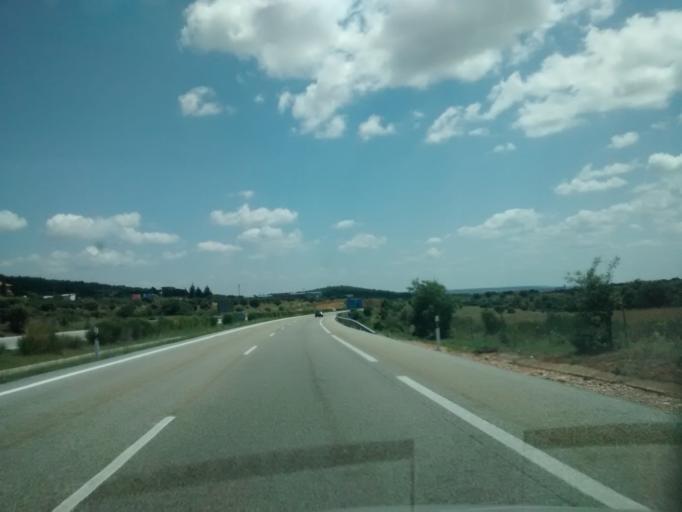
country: ES
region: Castille and Leon
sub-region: Provincia de Leon
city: Brazuelo
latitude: 42.4845
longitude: -6.1167
